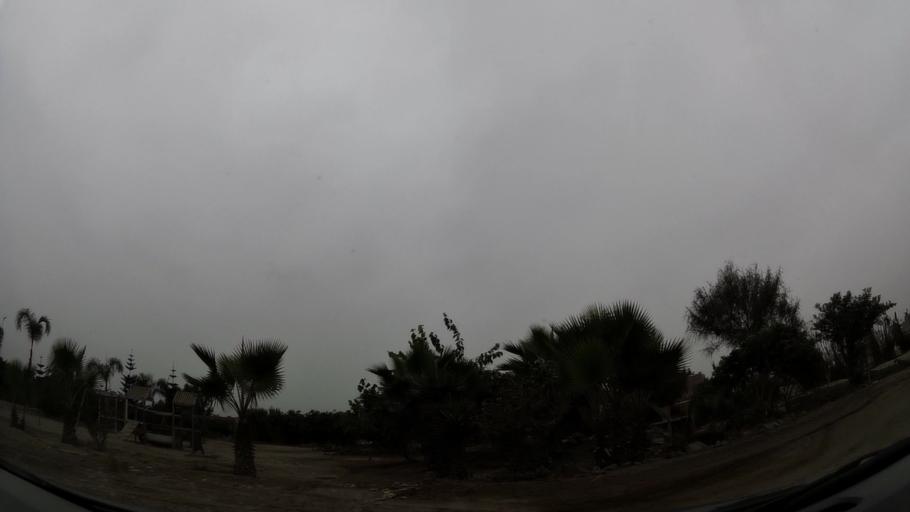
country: PE
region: Lima
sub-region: Lima
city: Punta Hermosa
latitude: -12.3291
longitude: -76.8275
